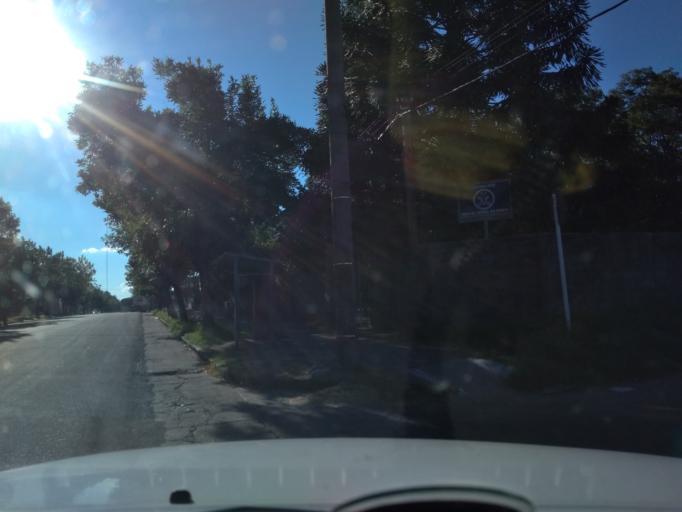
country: UY
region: Florida
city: Florida
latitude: -34.0987
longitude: -56.2273
